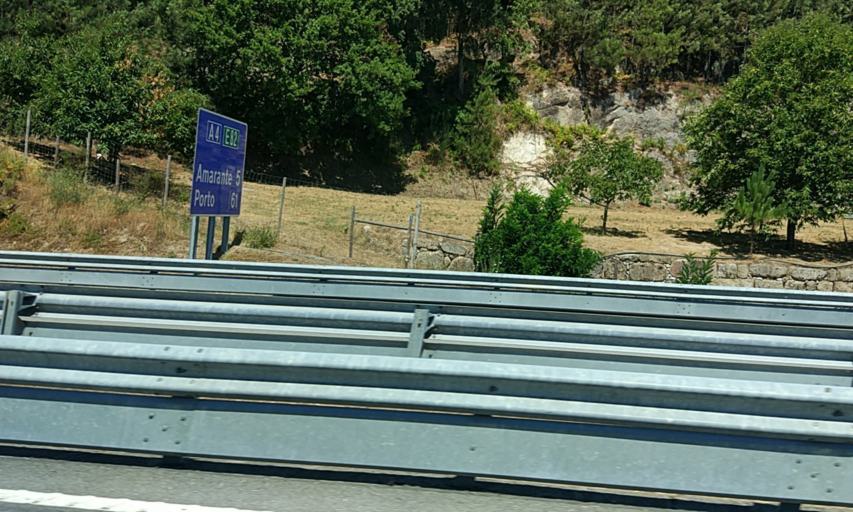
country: PT
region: Porto
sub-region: Amarante
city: Amarante
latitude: 41.2601
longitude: -8.0362
